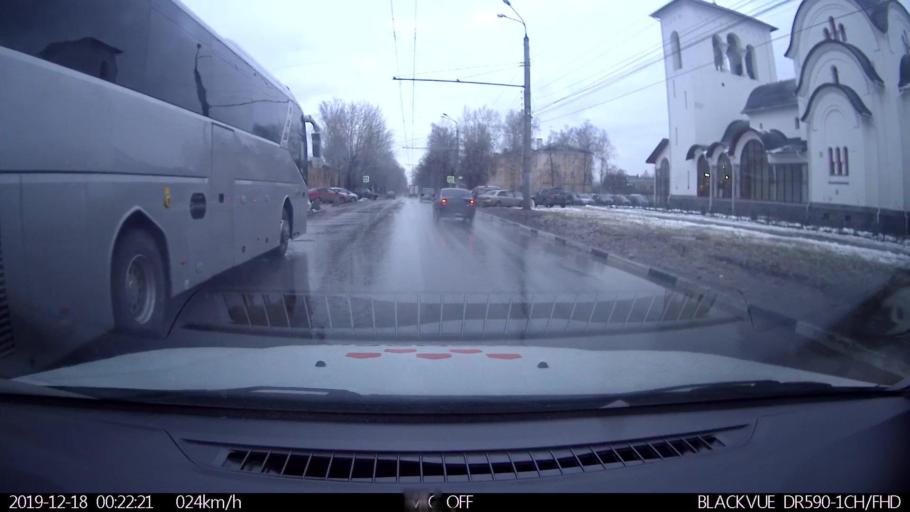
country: RU
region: Nizjnij Novgorod
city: Nizhniy Novgorod
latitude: 56.3311
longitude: 43.8844
